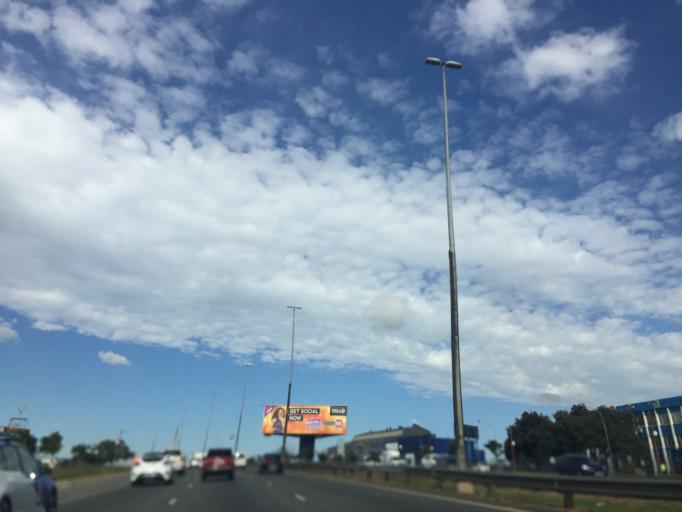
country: ZA
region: Gauteng
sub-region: City of Johannesburg Metropolitan Municipality
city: Modderfontein
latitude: -26.1292
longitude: 28.2122
